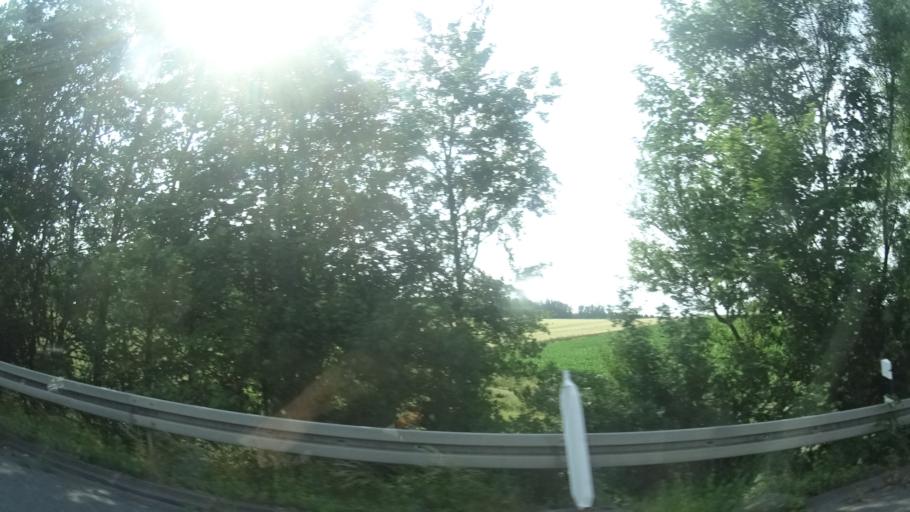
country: DE
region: Lower Saxony
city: Hillerse
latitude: 51.6797
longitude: 9.9262
